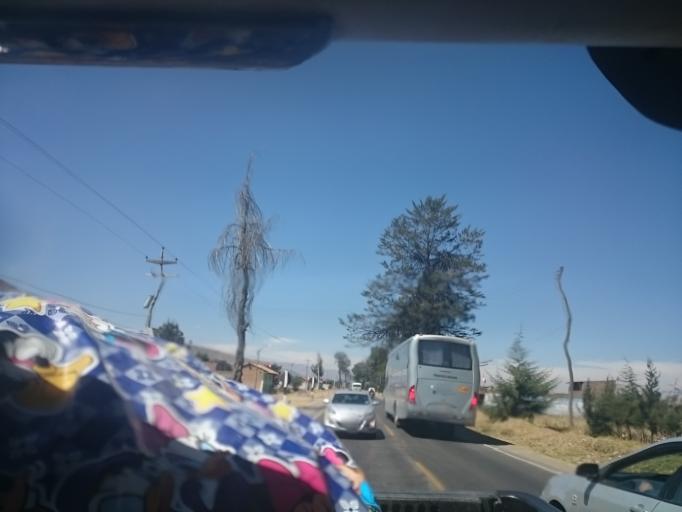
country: PE
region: Junin
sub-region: Provincia de Jauja
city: Huamali
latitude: -11.8128
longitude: -75.4253
